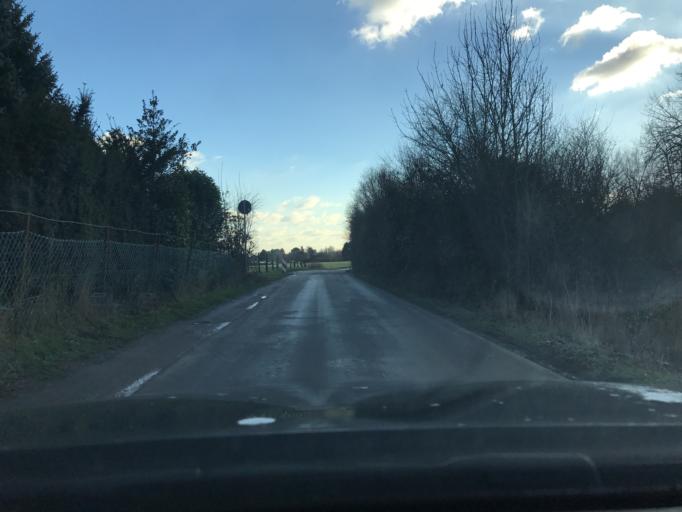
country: DE
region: North Rhine-Westphalia
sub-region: Regierungsbezirk Dusseldorf
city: Krefeld
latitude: 51.3598
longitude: 6.6046
